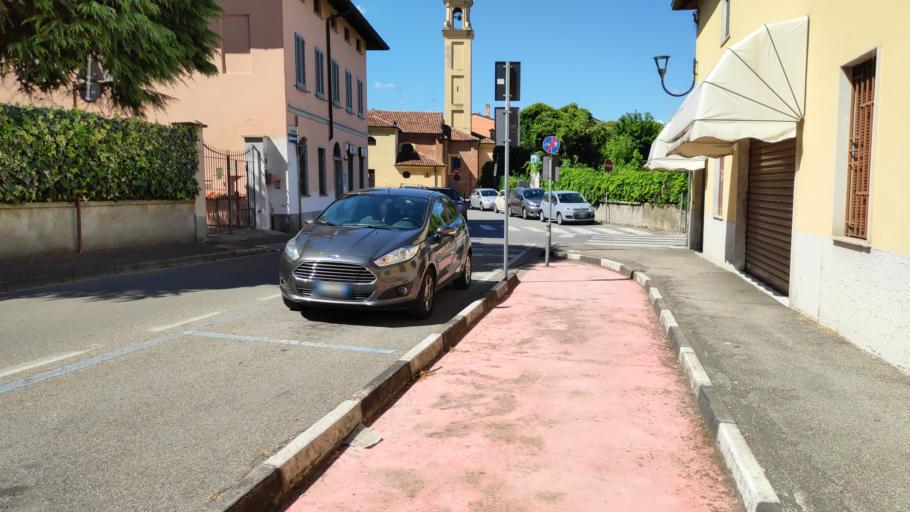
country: IT
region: Lombardy
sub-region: Citta metropolitana di Milano
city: Melzo
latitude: 45.4985
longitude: 9.4268
